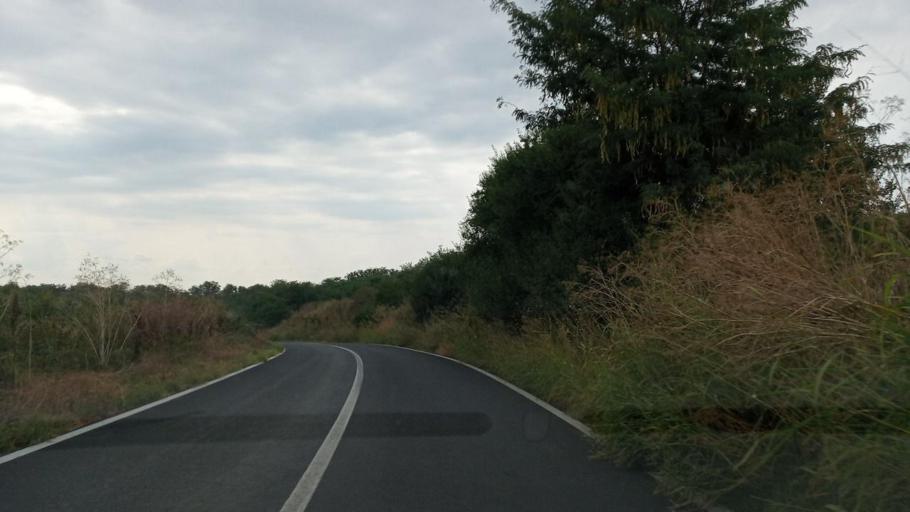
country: RO
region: Giurgiu
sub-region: Comuna Izvoarele
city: Isvoarele
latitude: 44.1696
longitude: 26.2697
